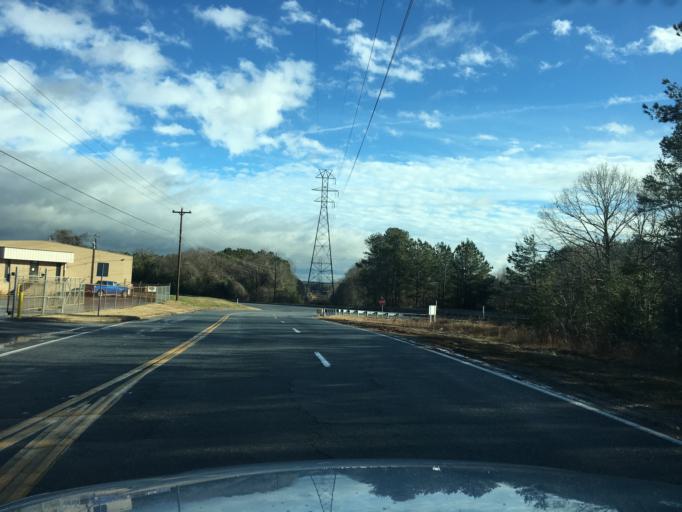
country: US
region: South Carolina
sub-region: Spartanburg County
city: Mayo
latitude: 35.0190
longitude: -81.8741
